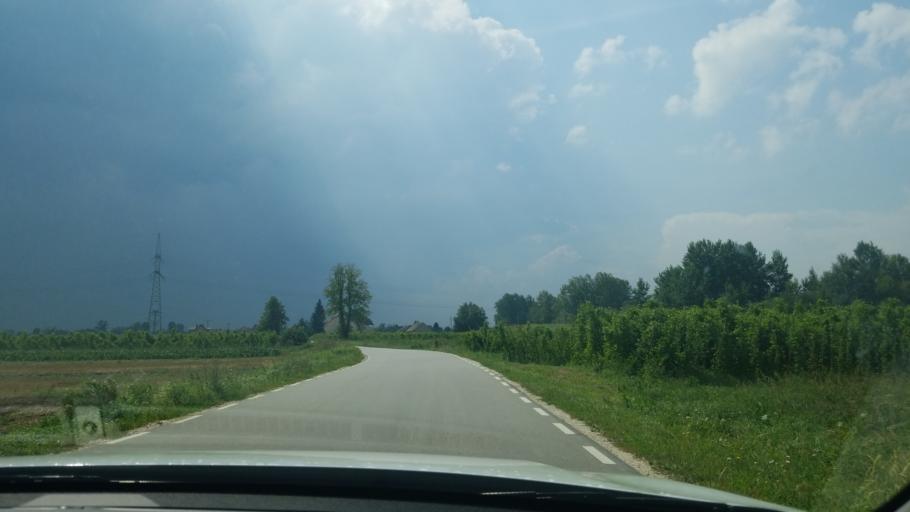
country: PL
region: Lesser Poland Voivodeship
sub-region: Powiat bochenski
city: Dziewin
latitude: 50.1091
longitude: 20.5147
